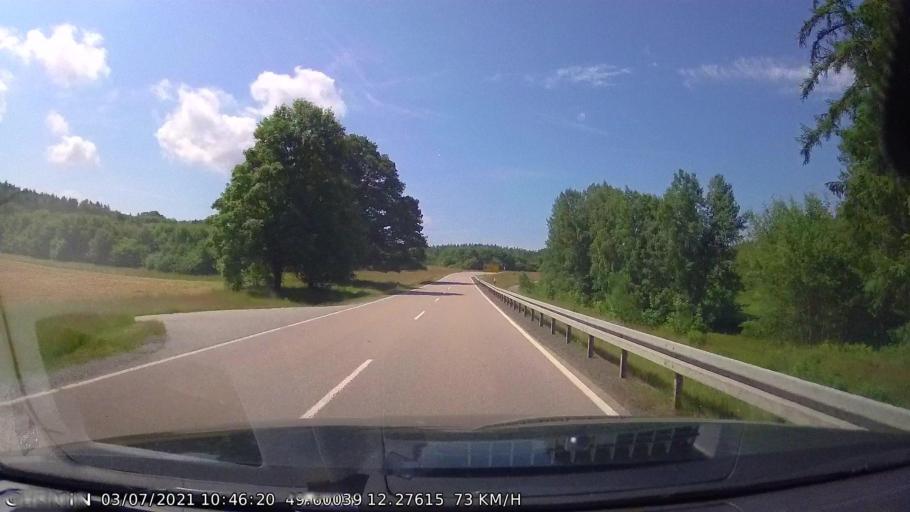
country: DE
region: Bavaria
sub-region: Upper Palatinate
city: Leuchtenberg
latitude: 49.6002
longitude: 12.2761
